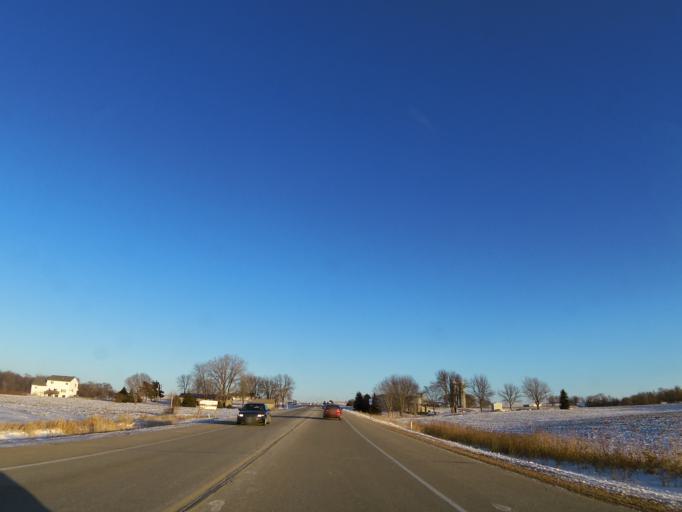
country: US
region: Minnesota
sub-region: Carver County
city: Chaska
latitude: 44.7619
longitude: -93.5649
